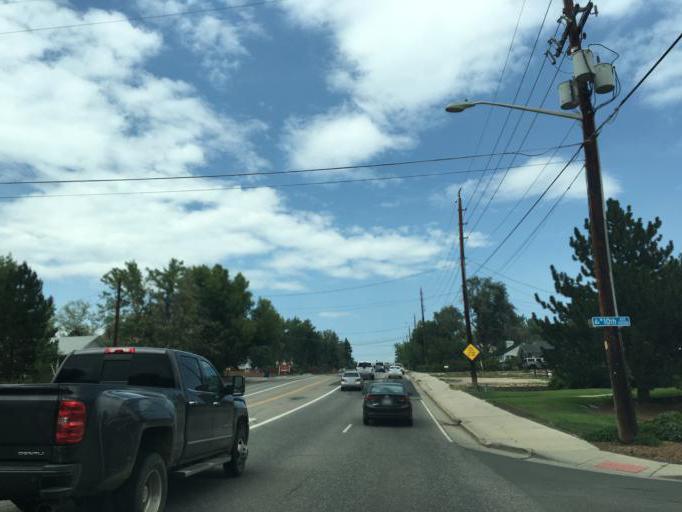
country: US
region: Colorado
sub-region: Jefferson County
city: Lakewood
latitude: 39.7331
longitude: -105.1096
